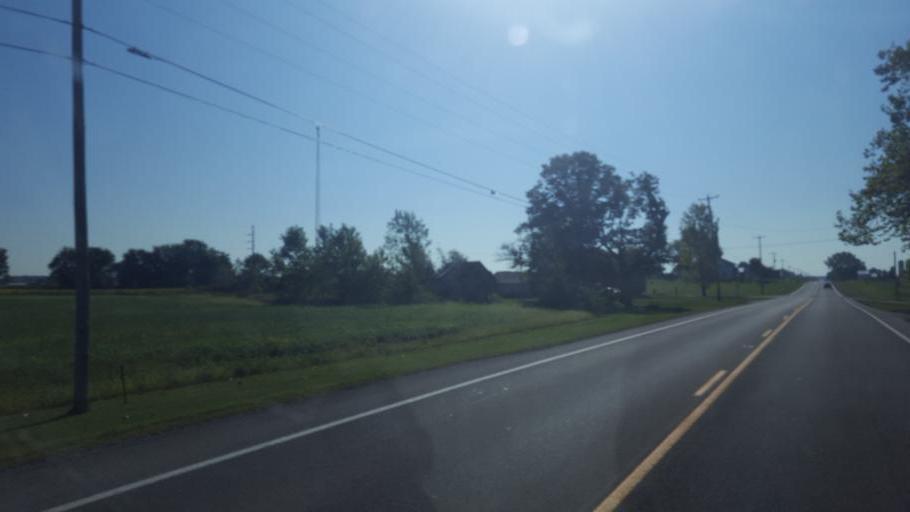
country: US
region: Ohio
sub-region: Hardin County
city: Kenton
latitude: 40.5809
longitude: -83.5590
